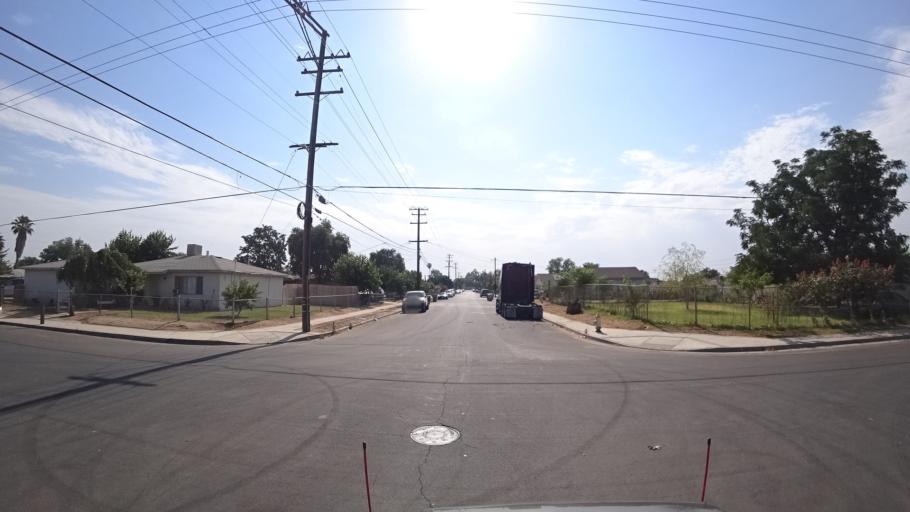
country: US
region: California
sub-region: Fresno County
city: West Park
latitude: 36.7186
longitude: -119.8157
